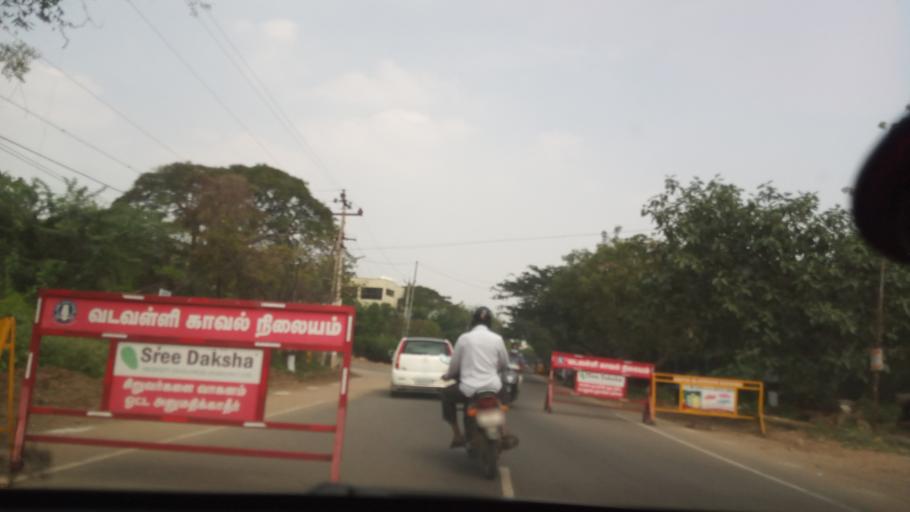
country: IN
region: Tamil Nadu
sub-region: Coimbatore
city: Perur
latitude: 11.0237
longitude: 76.8894
